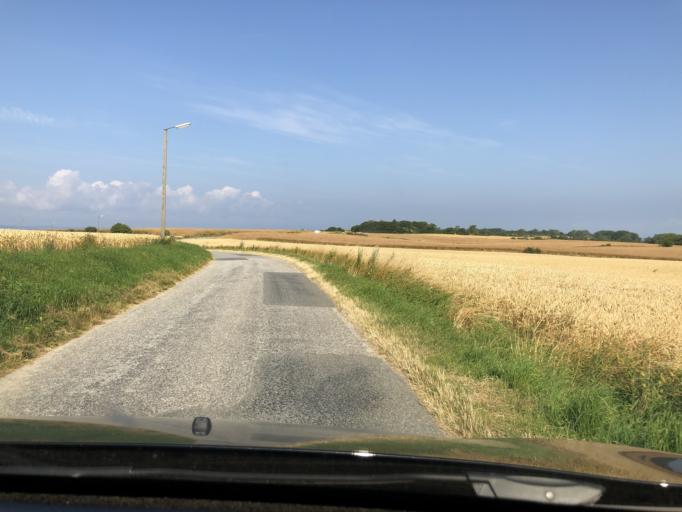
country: DK
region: South Denmark
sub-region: Faaborg-Midtfyn Kommune
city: Faaborg
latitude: 54.9461
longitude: 10.2396
